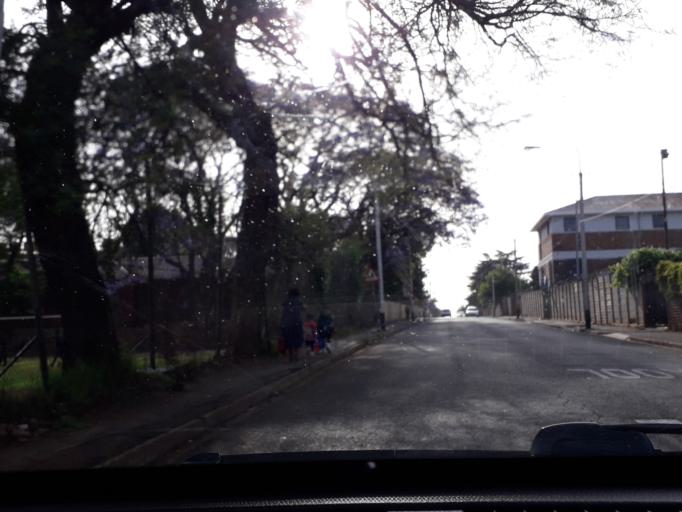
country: ZA
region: Gauteng
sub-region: City of Johannesburg Metropolitan Municipality
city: Johannesburg
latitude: -26.1567
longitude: 28.0877
